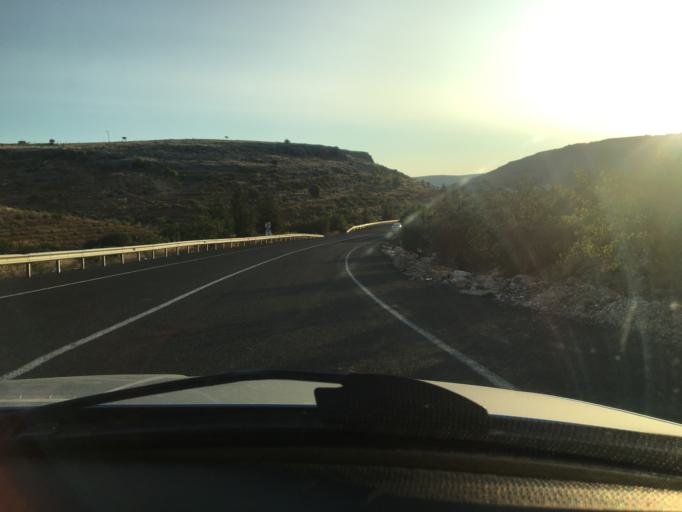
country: TR
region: Sanliurfa
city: Halfeti
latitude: 37.2236
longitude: 37.9594
